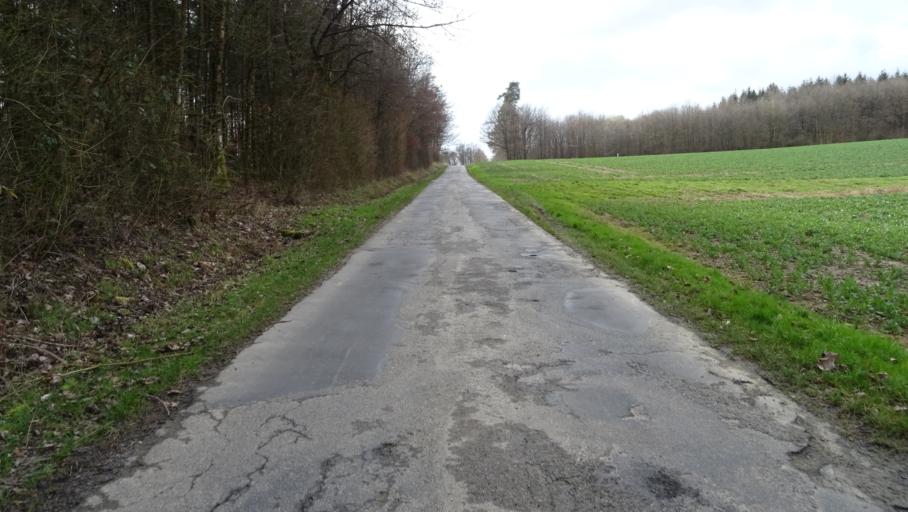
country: DE
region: Baden-Wuerttemberg
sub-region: Karlsruhe Region
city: Limbach
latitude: 49.4379
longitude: 9.2688
